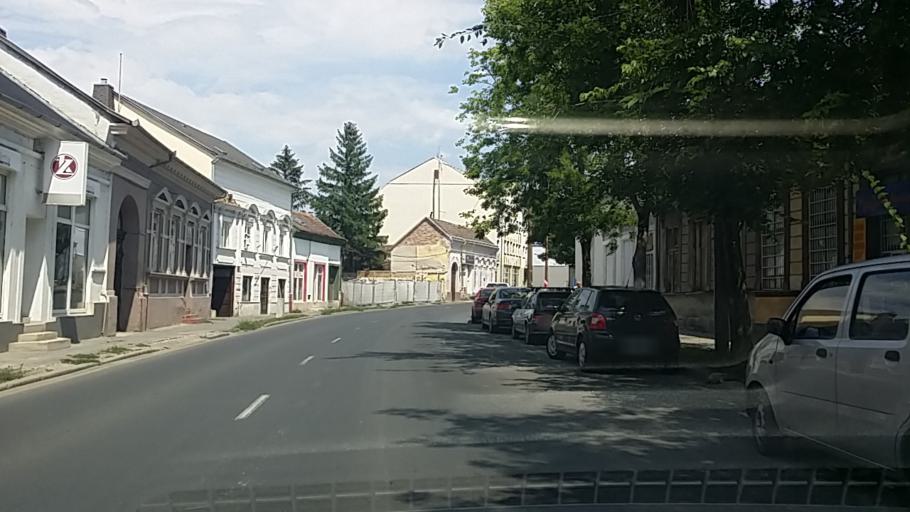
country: HU
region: Zala
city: Nagykanizsa
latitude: 46.4542
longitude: 16.9830
